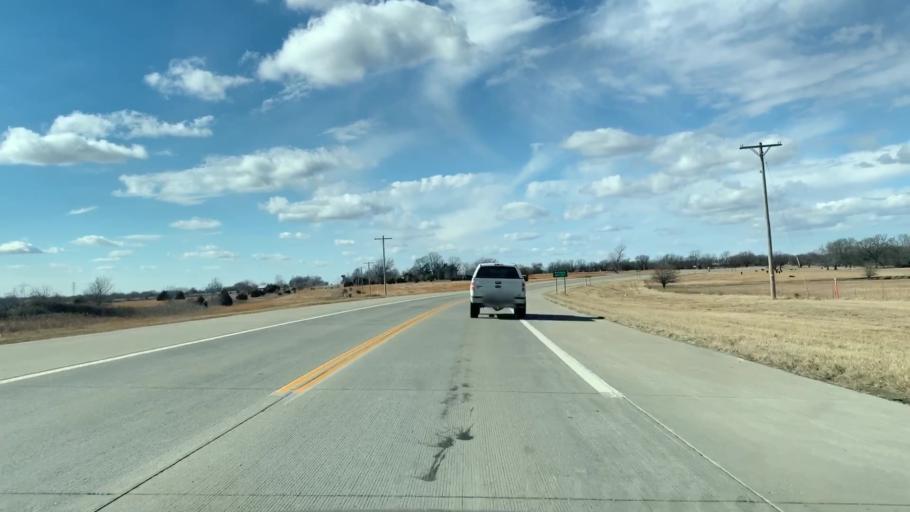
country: US
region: Kansas
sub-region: Labette County
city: Parsons
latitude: 37.3404
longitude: -95.1767
